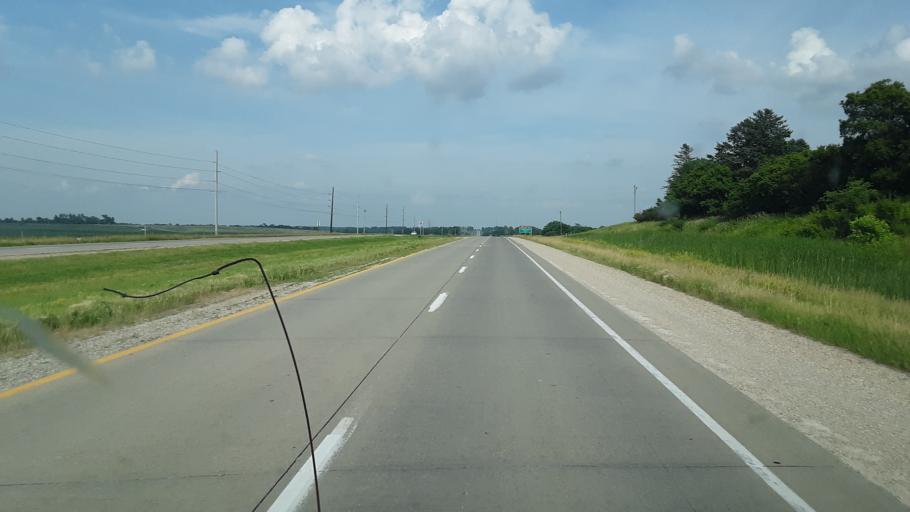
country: US
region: Iowa
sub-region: Marshall County
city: Marshalltown
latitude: 42.0075
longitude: -92.9952
